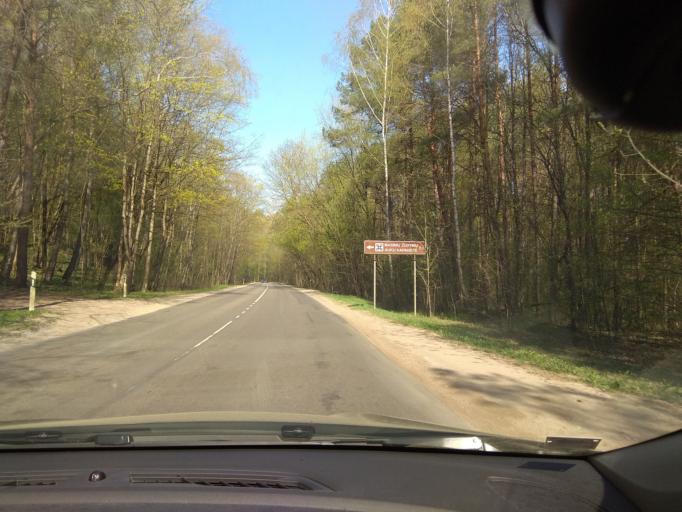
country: LT
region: Vilnius County
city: Lazdynai
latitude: 54.6543
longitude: 25.1817
